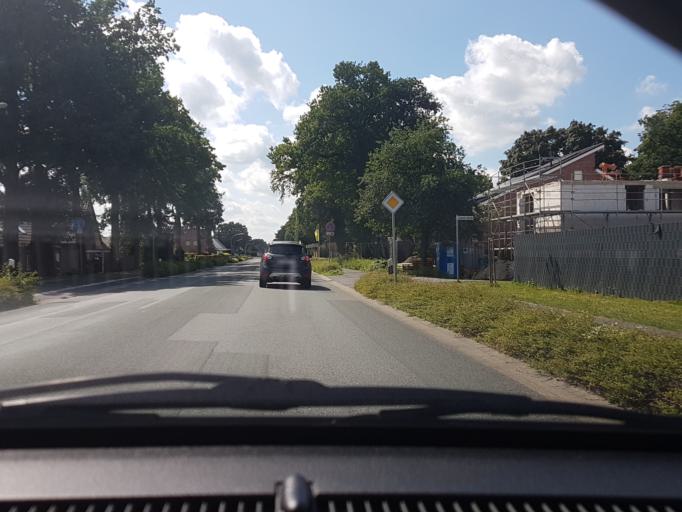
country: DE
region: North Rhine-Westphalia
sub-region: Regierungsbezirk Munster
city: Neuenkirchen
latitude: 52.2356
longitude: 7.3616
